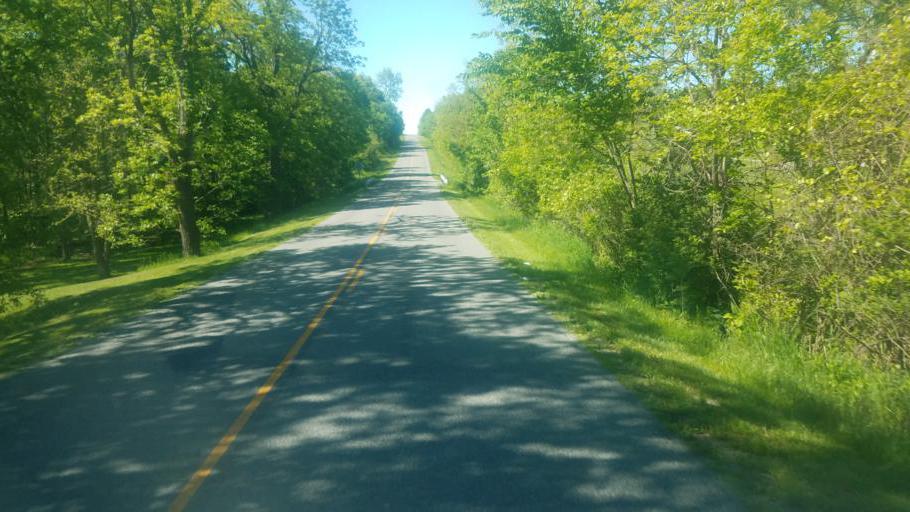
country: US
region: Ohio
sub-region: Logan County
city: Northwood
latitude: 40.4255
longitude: -83.7548
